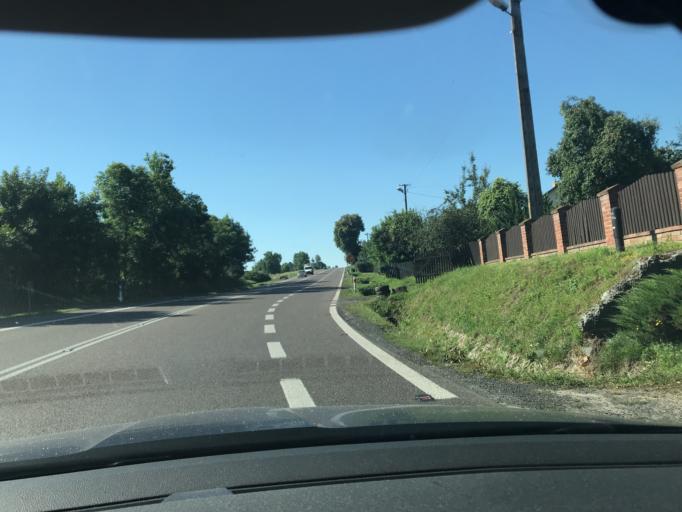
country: PL
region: Lublin Voivodeship
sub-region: Powiat krasnostawski
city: Izbica
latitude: 50.8845
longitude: 23.1500
